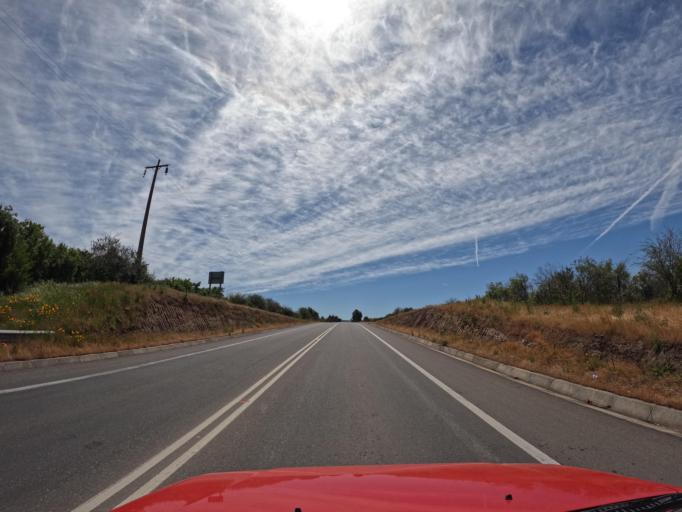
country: CL
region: Maule
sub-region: Provincia de Talca
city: Talca
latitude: -35.2770
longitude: -71.5383
